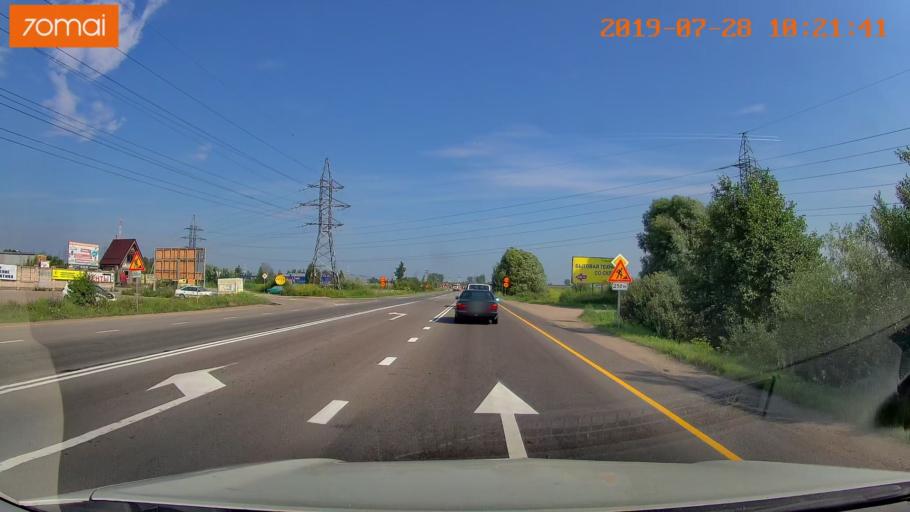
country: RU
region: Kaliningrad
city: Maloye Isakovo
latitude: 54.7585
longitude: 20.5637
